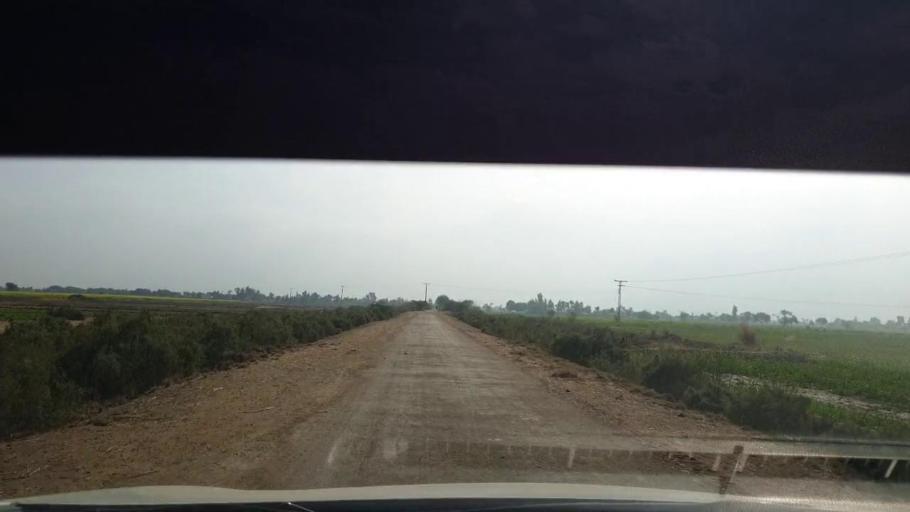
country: PK
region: Sindh
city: Berani
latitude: 25.7641
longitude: 68.8764
